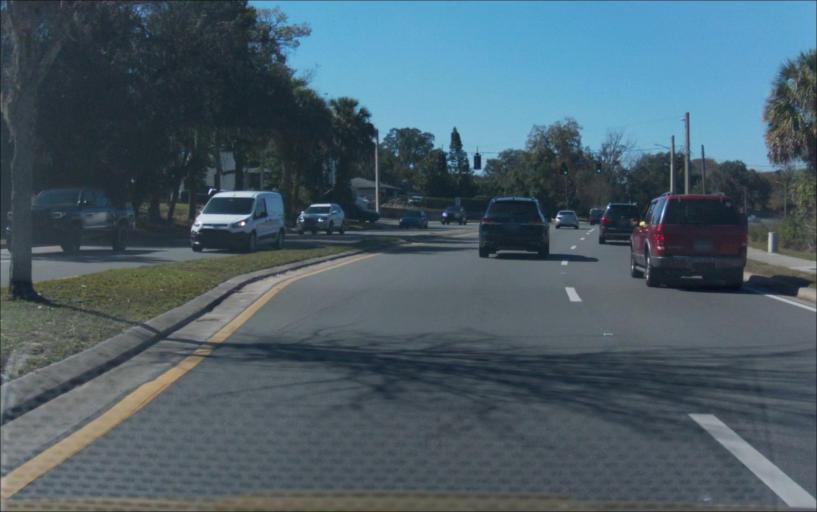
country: US
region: Florida
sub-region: Orange County
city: Winter Park
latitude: 28.6259
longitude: -81.3297
